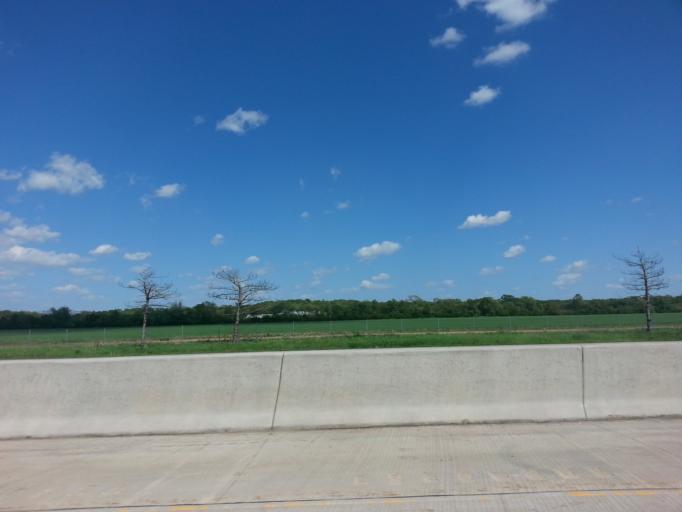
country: US
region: Illinois
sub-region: Winnebago County
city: South Beloit
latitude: 42.4656
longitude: -88.9952
